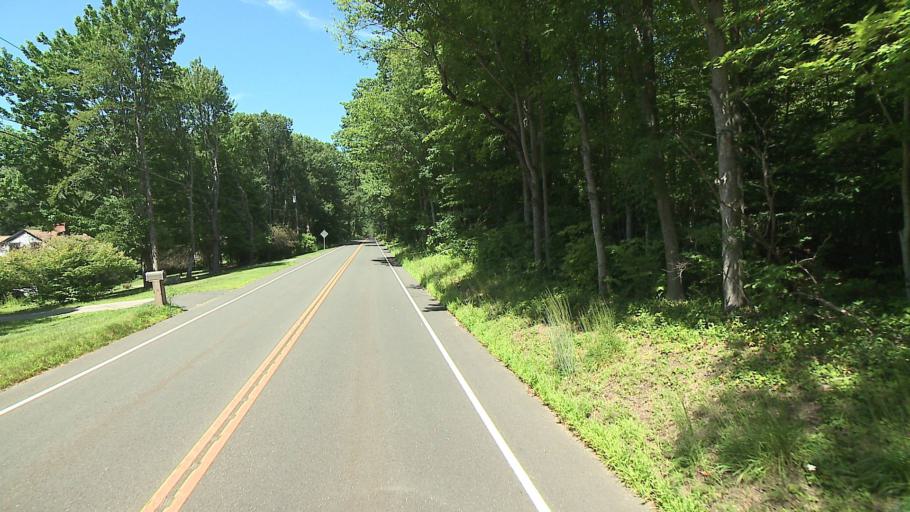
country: US
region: Connecticut
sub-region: Litchfield County
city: New Hartford Center
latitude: 41.9382
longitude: -72.9706
